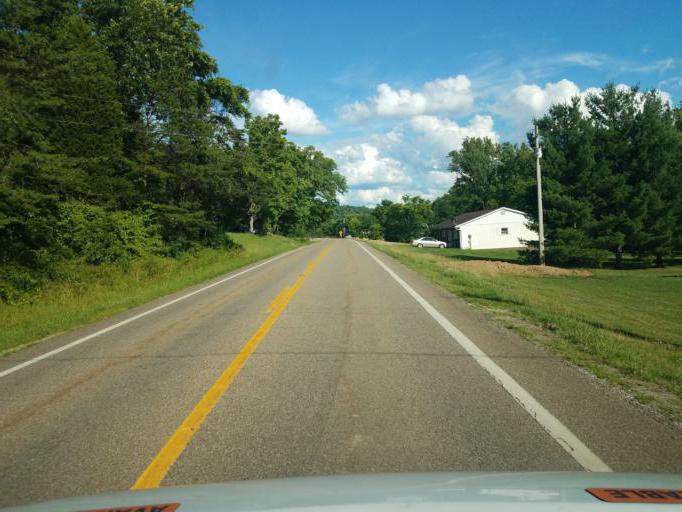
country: US
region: Ohio
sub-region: Gallia County
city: Gallipolis
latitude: 38.7966
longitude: -82.2850
